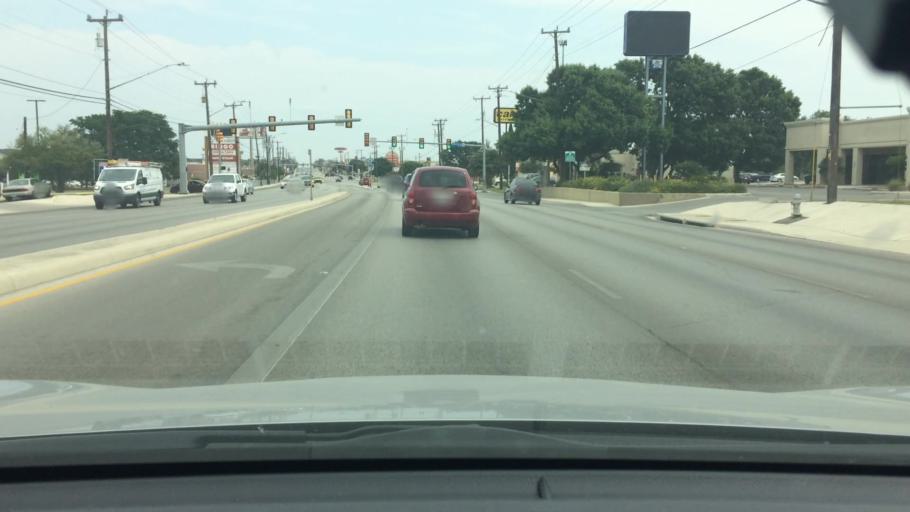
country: US
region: Texas
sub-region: Bexar County
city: Leon Valley
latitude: 29.4702
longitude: -98.6509
